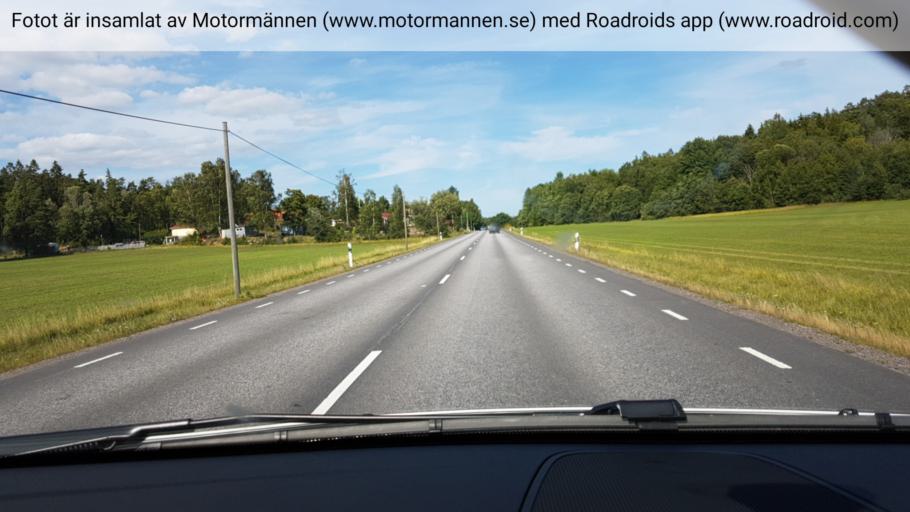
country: SE
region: Stockholm
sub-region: Sodertalje Kommun
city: Pershagen
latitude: 59.0921
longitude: 17.6169
